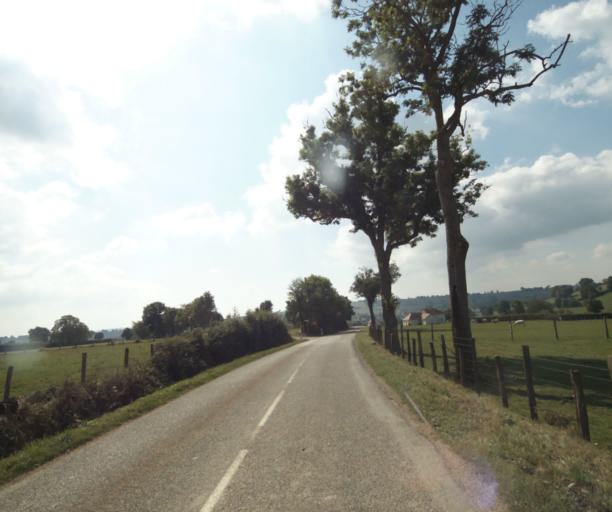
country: FR
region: Bourgogne
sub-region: Departement de Saone-et-Loire
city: Charolles
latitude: 46.3733
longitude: 4.2468
